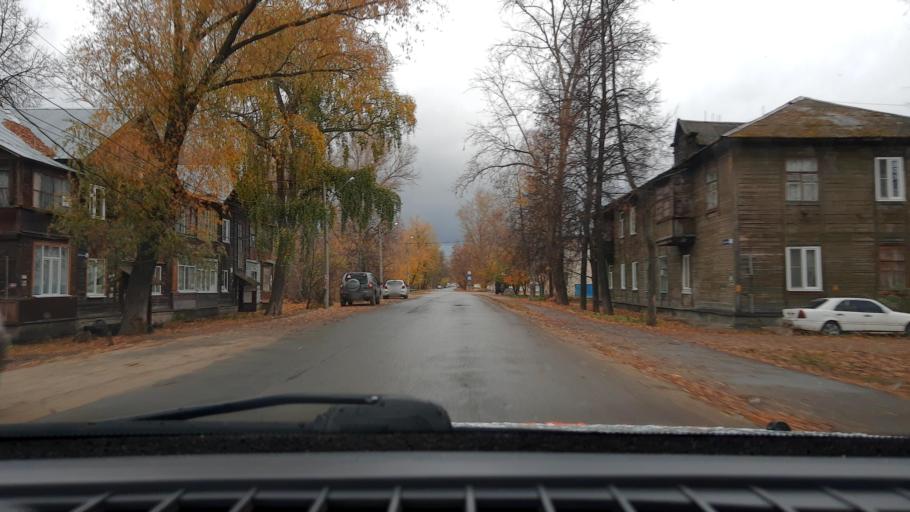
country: RU
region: Nizjnij Novgorod
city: Nizhniy Novgorod
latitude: 56.3086
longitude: 43.8908
